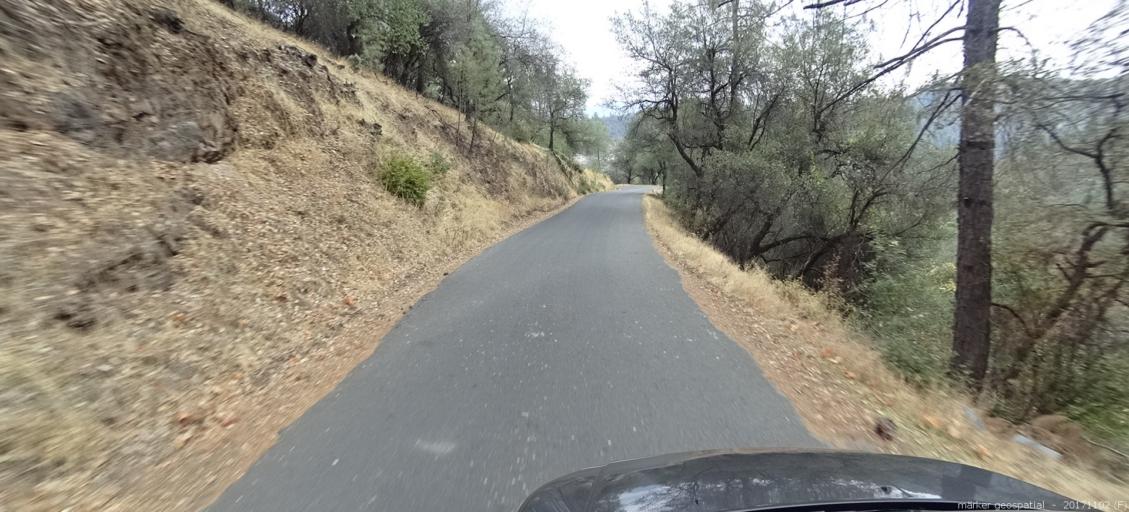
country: US
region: California
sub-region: Shasta County
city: Bella Vista
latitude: 40.7516
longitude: -122.2460
